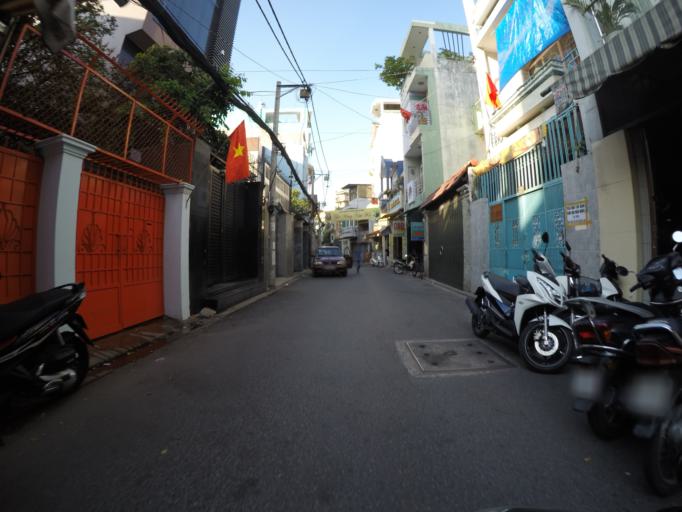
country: VN
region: Ho Chi Minh City
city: Quan Phu Nhuan
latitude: 10.7978
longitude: 106.6842
